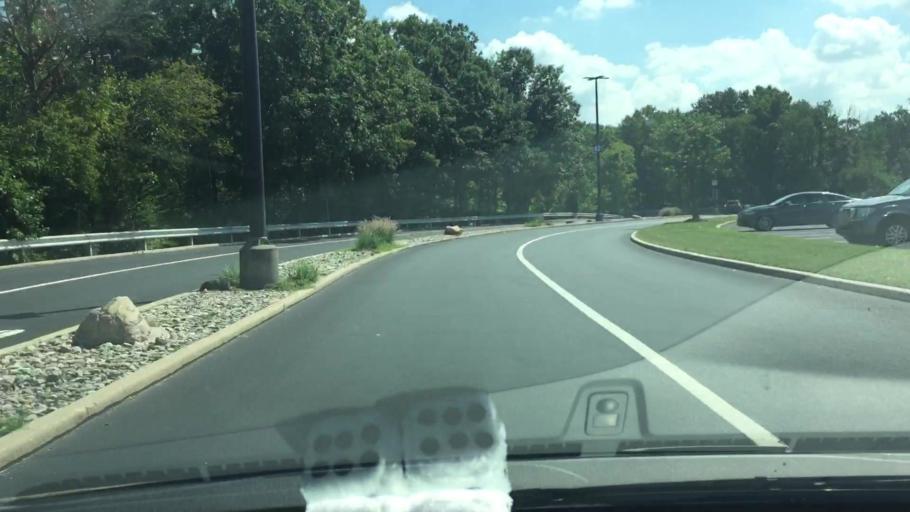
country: US
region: New Jersey
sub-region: Camden County
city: Glendora
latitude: 39.8294
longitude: -75.0961
